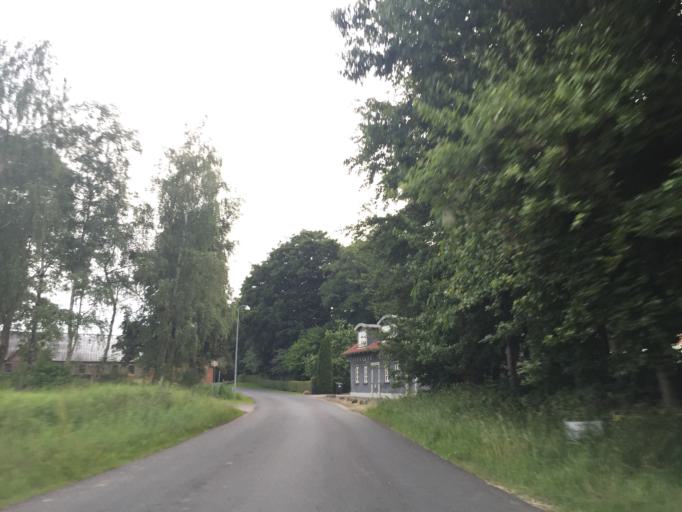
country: DK
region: Central Jutland
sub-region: Silkeborg Kommune
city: Kjellerup
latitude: 56.2443
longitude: 9.4935
